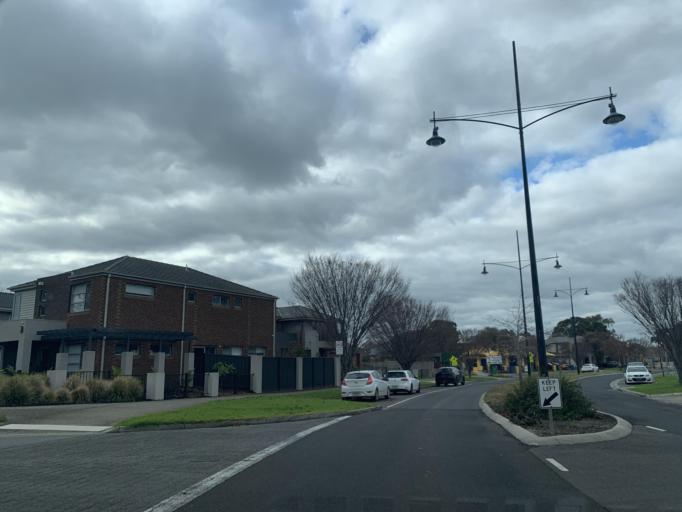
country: AU
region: Victoria
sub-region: Whittlesea
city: Epping
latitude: -37.6284
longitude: 145.0233
